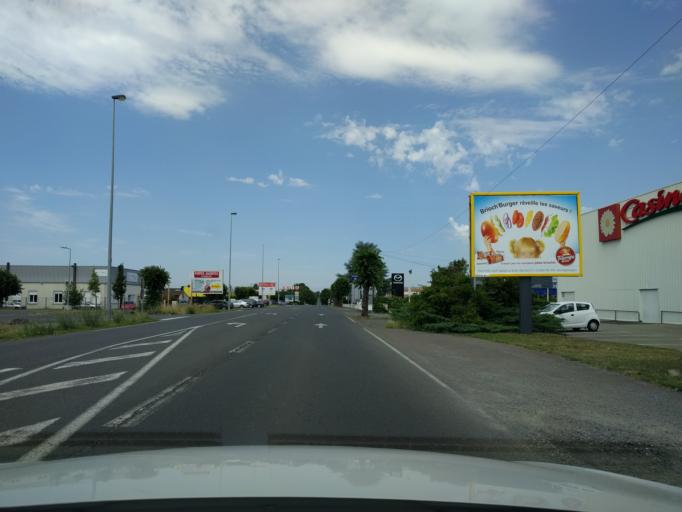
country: FR
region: Poitou-Charentes
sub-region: Departement des Deux-Sevres
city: Niort
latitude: 46.3411
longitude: -0.4896
